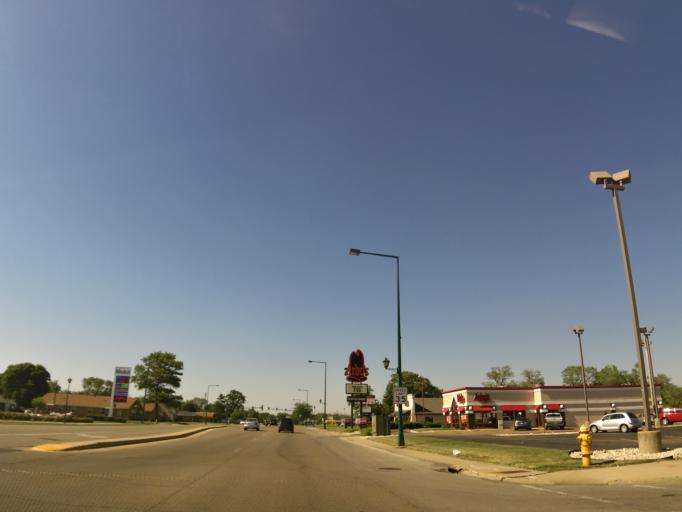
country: US
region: Illinois
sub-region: Winnebago County
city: Loves Park
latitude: 42.3202
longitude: -89.0579
